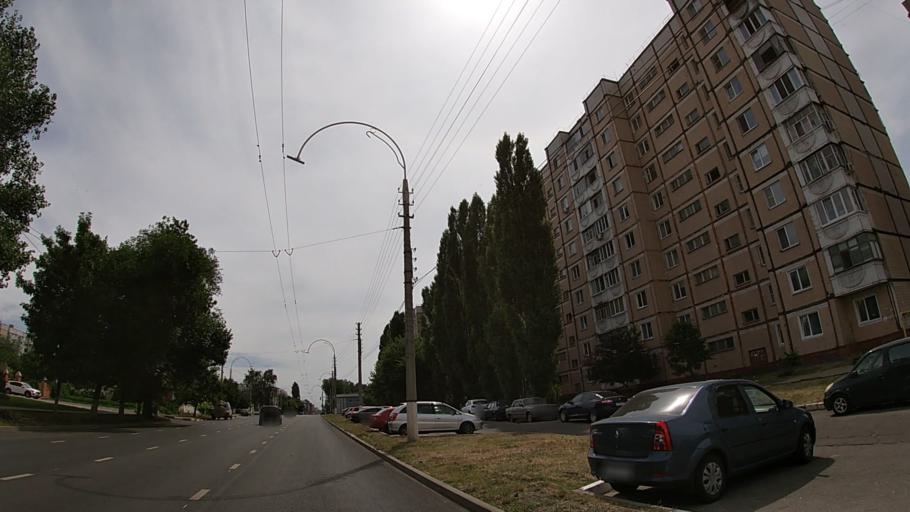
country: RU
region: Belgorod
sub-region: Belgorodskiy Rayon
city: Belgorod
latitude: 50.5999
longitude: 36.5707
